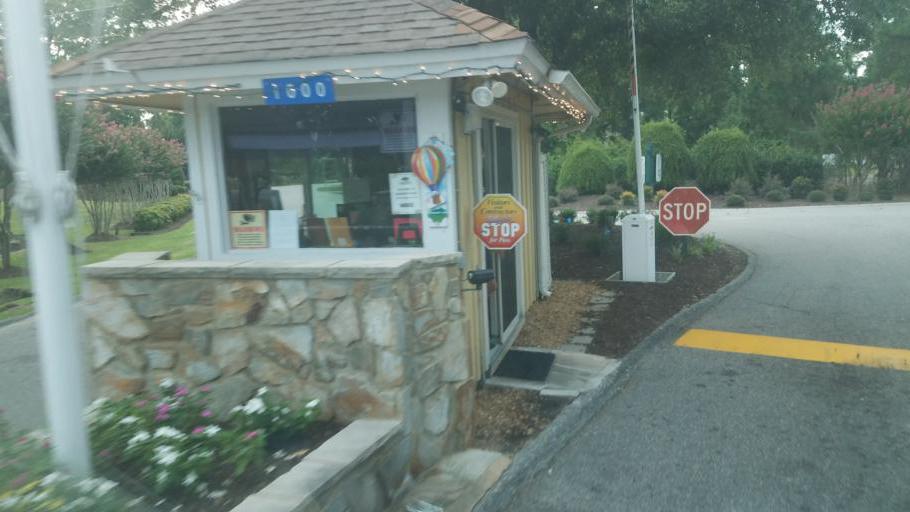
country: US
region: North Carolina
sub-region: Dare County
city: Southern Shores
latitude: 36.0945
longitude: -75.7409
